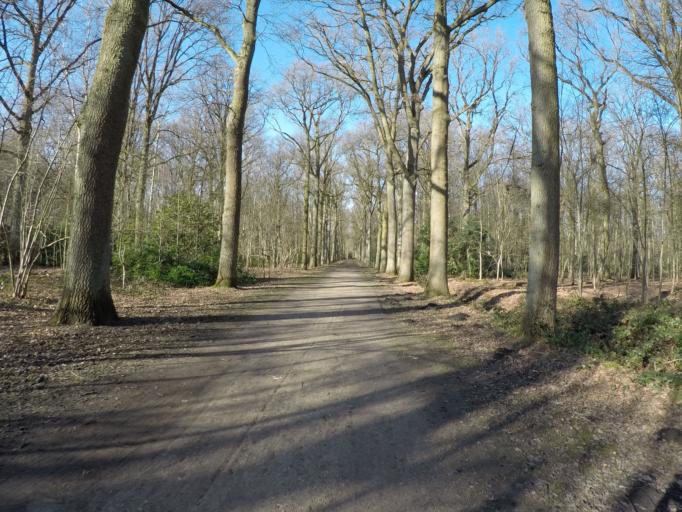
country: BE
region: Flanders
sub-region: Provincie Antwerpen
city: Brasschaat
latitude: 51.2806
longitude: 4.5013
